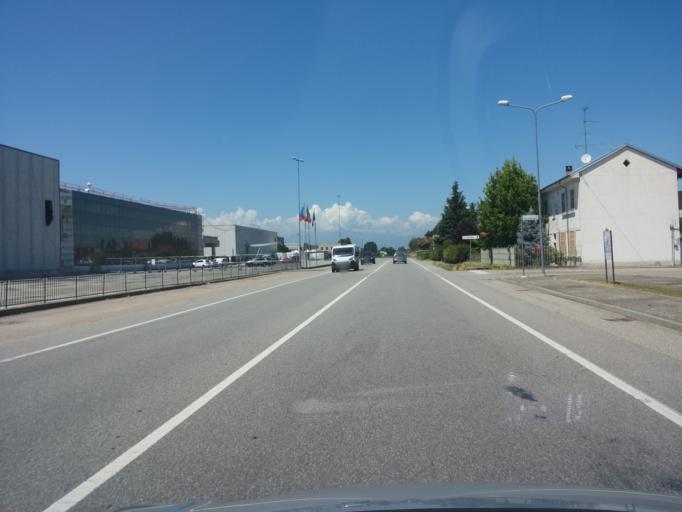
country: IT
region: Piedmont
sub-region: Provincia di Vercelli
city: Caresanablot
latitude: 45.3626
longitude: 8.3838
